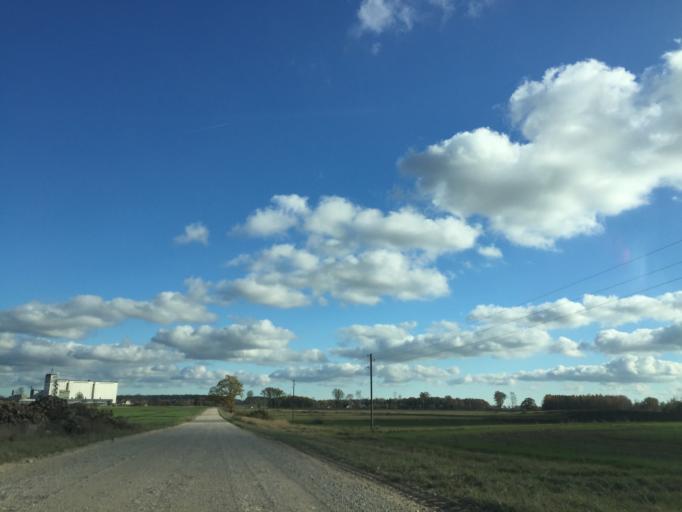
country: LV
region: Tukuma Rajons
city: Tukums
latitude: 56.9520
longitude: 23.0865
